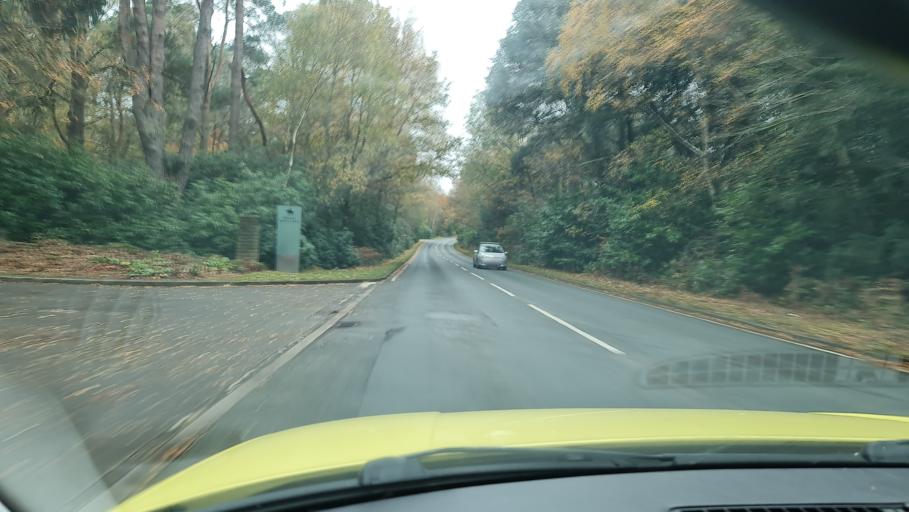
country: GB
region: England
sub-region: Hampshire
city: Aldershot
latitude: 51.2514
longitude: -0.7811
